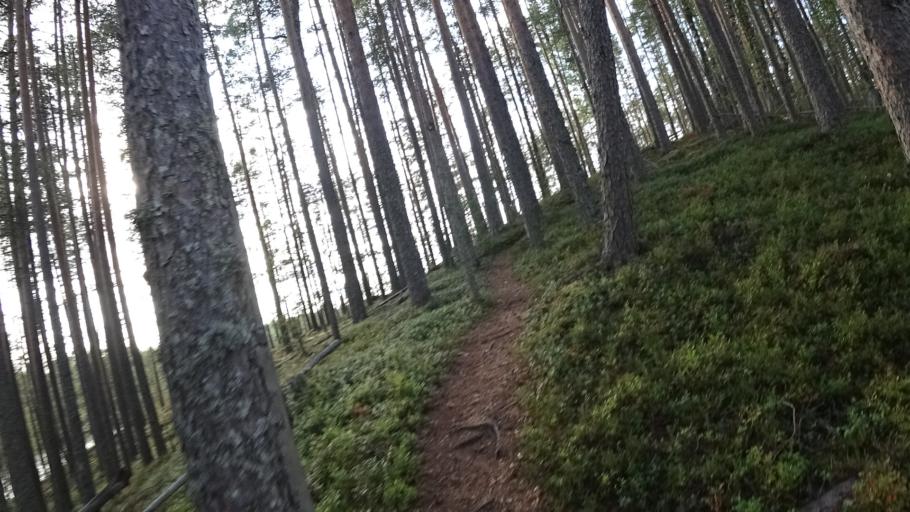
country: FI
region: North Karelia
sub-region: Joensuu
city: Ilomantsi
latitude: 62.5679
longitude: 31.1812
